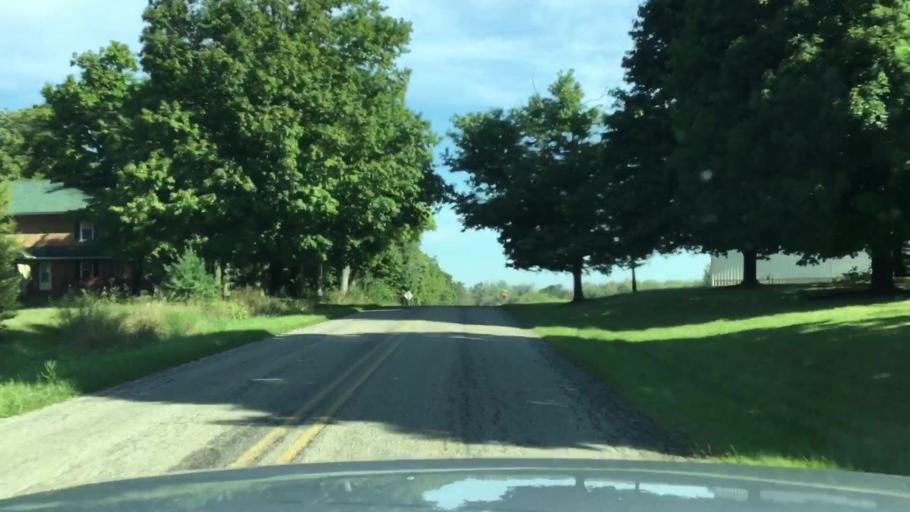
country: US
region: Michigan
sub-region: Lenawee County
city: Hudson
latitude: 41.8993
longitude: -84.4204
